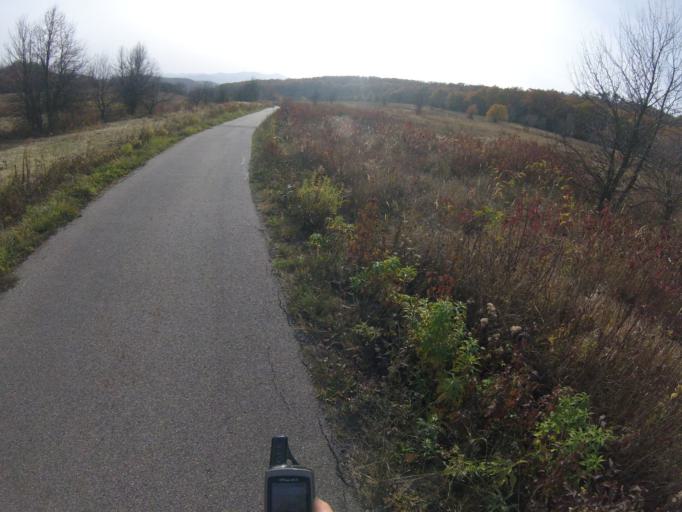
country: HU
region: Borsod-Abauj-Zemplen
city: Gonc
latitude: 48.5230
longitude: 21.4579
